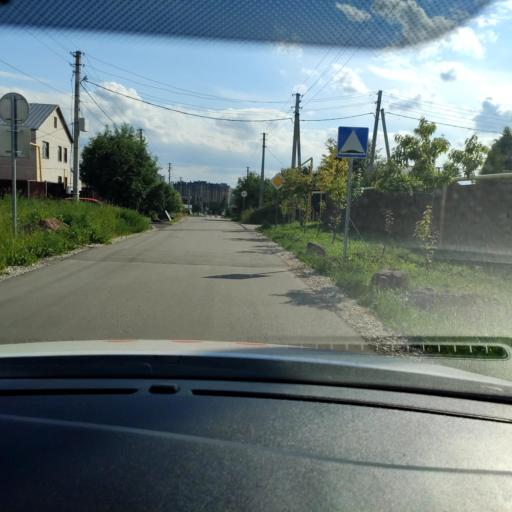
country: RU
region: Tatarstan
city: Vysokaya Gora
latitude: 55.8072
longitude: 49.2520
